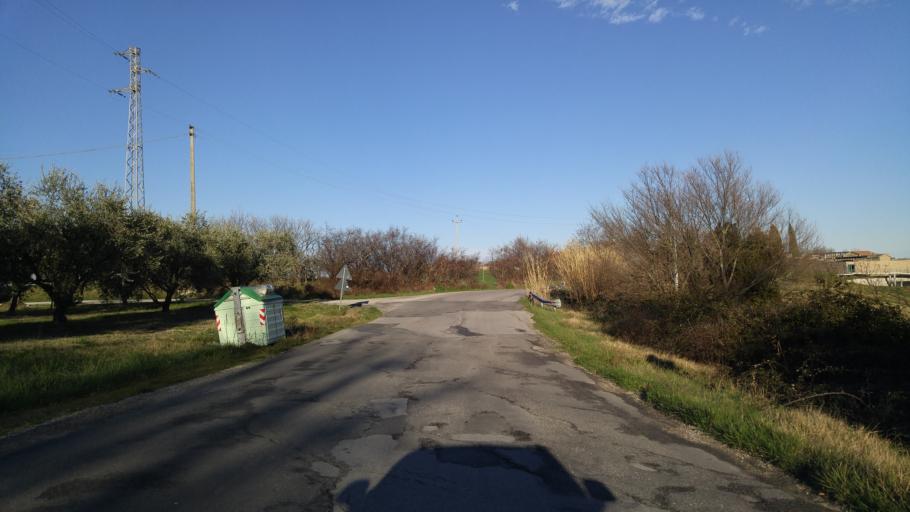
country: IT
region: The Marches
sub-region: Provincia di Pesaro e Urbino
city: San Giorgio di Pesaro
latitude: 43.7502
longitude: 13.0063
